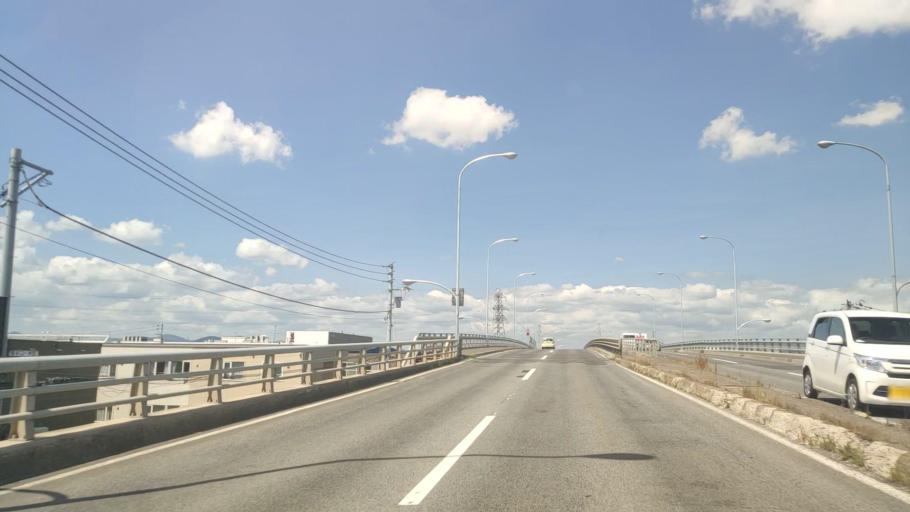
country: JP
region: Hokkaido
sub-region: Asahikawa-shi
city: Asahikawa
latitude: 43.7928
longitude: 142.4021
